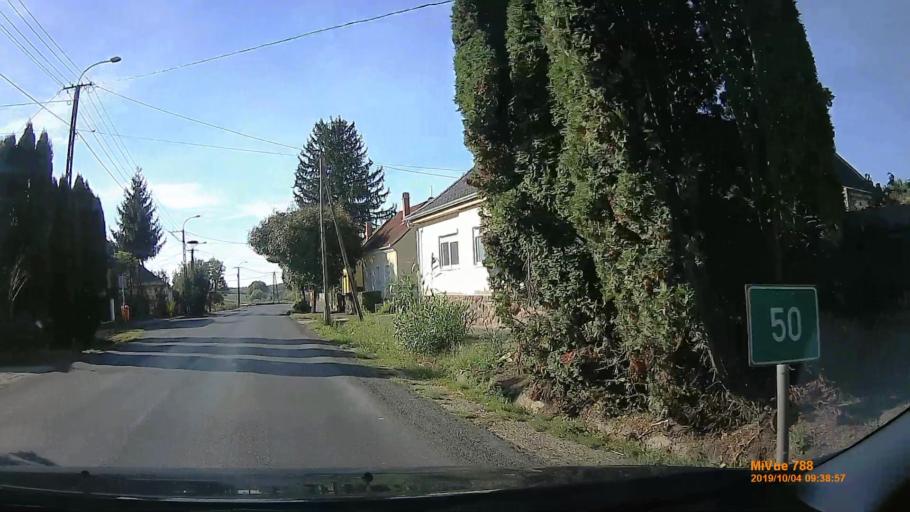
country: HU
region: Somogy
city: Kaposvar
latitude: 46.4548
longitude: 17.8054
